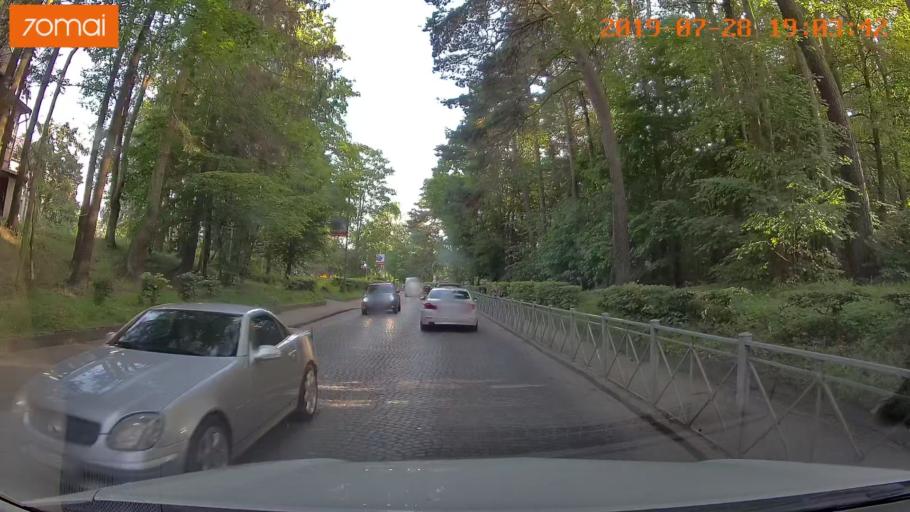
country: RU
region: Kaliningrad
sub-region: Gorod Svetlogorsk
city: Svetlogorsk
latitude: 54.9350
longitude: 20.1616
